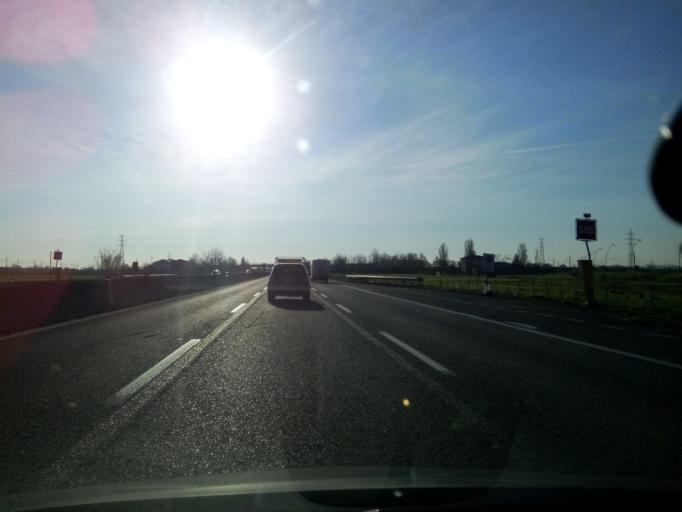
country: IT
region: Emilia-Romagna
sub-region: Provincia di Parma
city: Baganzola
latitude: 44.8451
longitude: 10.3170
